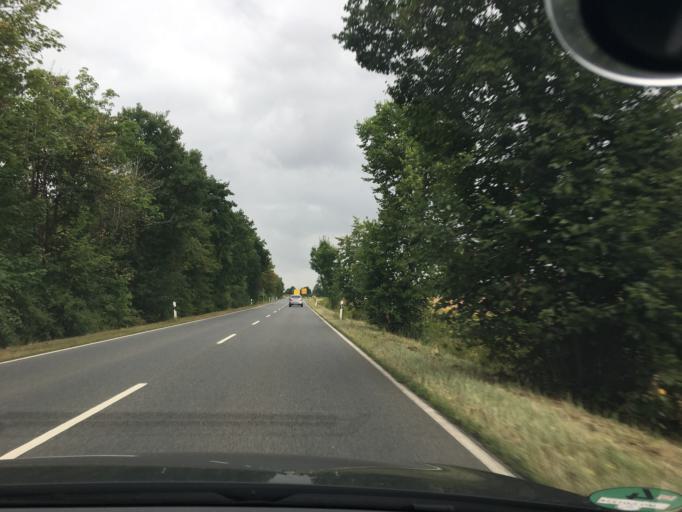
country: DE
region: North Rhine-Westphalia
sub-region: Regierungsbezirk Koln
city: Vettweiss
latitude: 50.7418
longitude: 6.6332
